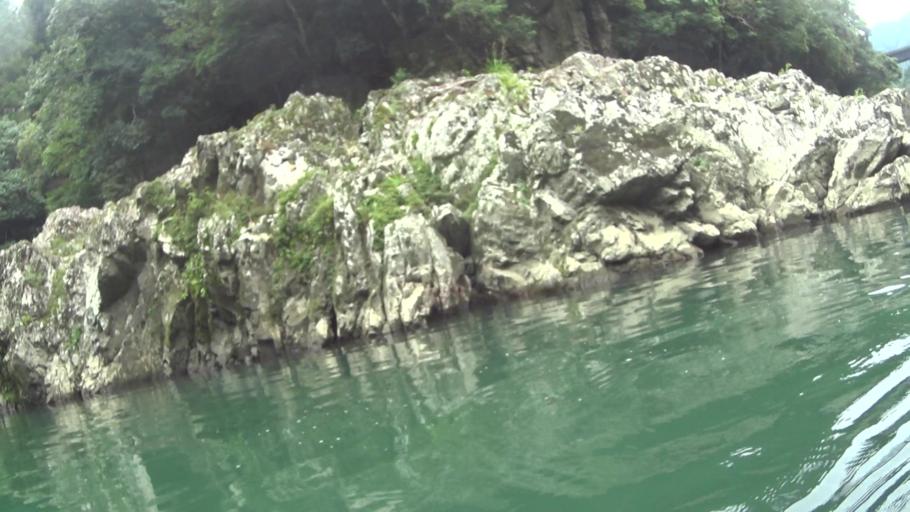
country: JP
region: Kyoto
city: Kameoka
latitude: 35.0245
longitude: 135.6313
